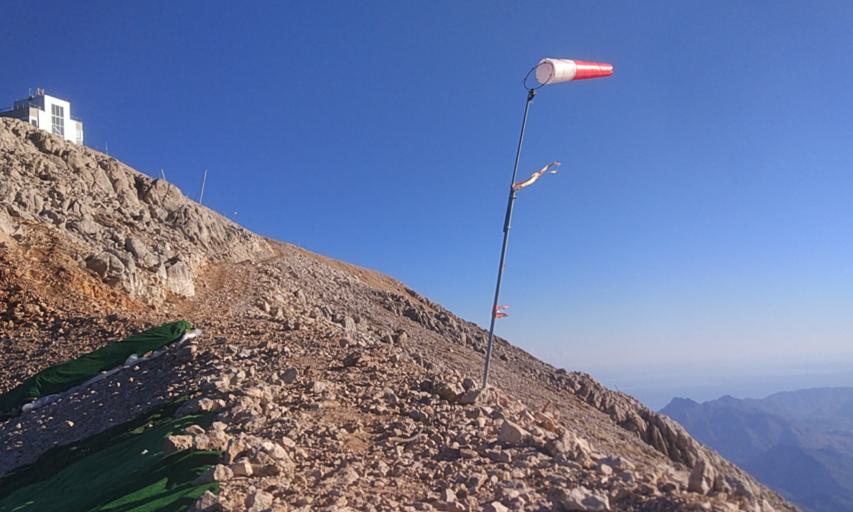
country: TR
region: Antalya
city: Tekirova
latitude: 36.5378
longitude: 30.4402
